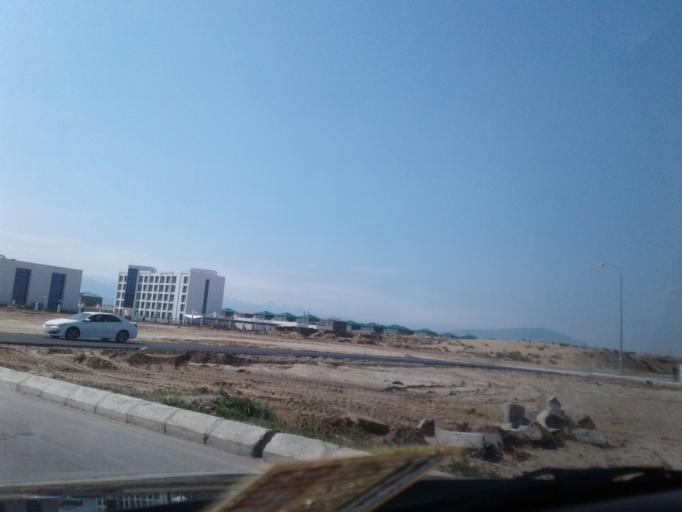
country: TM
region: Ahal
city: Ashgabat
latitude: 38.0091
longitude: 58.3993
